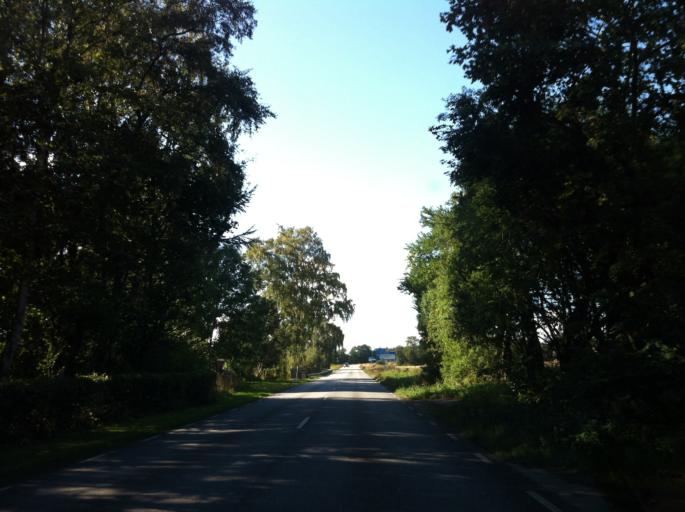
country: SE
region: Skane
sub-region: Hoors Kommun
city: Loberod
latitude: 55.7302
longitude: 13.4770
